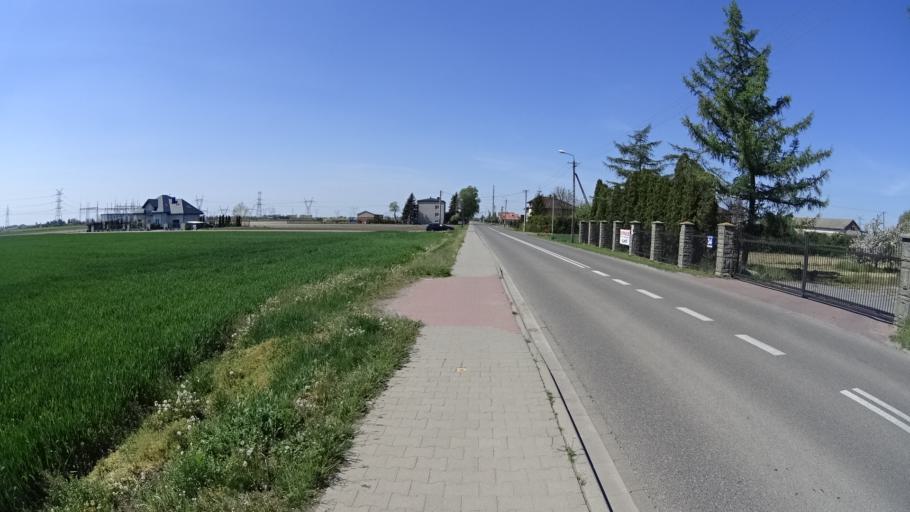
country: PL
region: Masovian Voivodeship
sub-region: Powiat warszawski zachodni
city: Ozarow Mazowiecki
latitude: 52.2309
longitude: 20.7483
